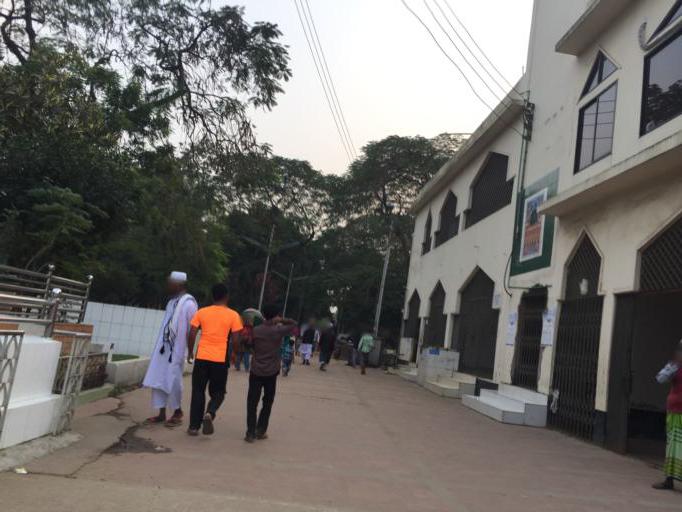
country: BD
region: Dhaka
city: Azimpur
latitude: 23.7951
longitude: 90.3463
